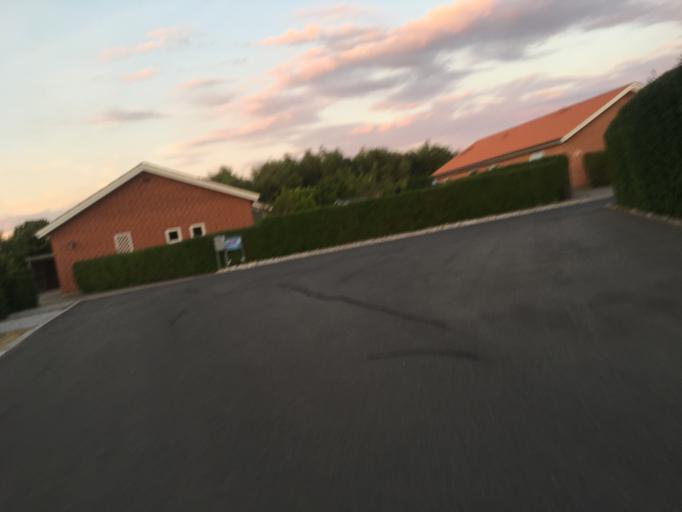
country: DK
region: Central Jutland
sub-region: Syddjurs Kommune
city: Hornslet
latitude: 56.3222
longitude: 10.3285
